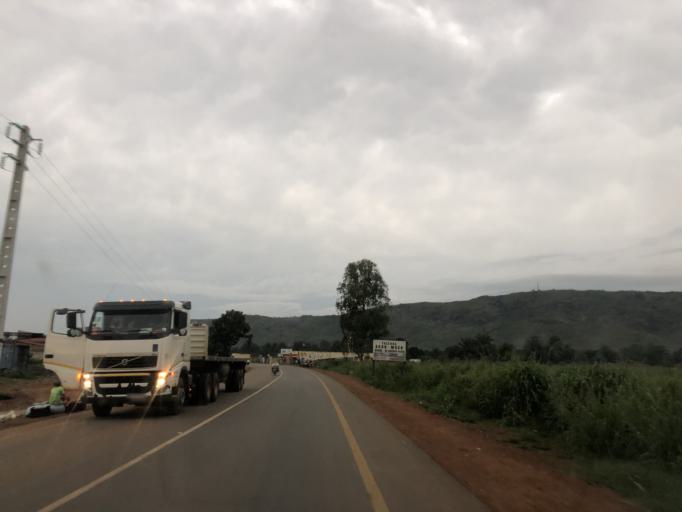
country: AO
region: Cuanza Sul
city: Uacu Cungo
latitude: -11.3465
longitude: 15.1043
